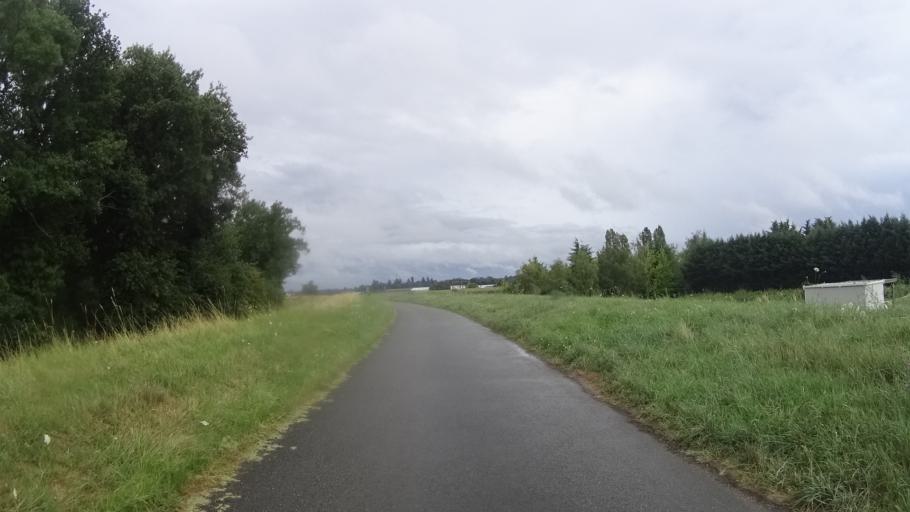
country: FR
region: Centre
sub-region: Departement du Loiret
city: Saint-Denis-en-Val
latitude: 47.8890
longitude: 1.9804
